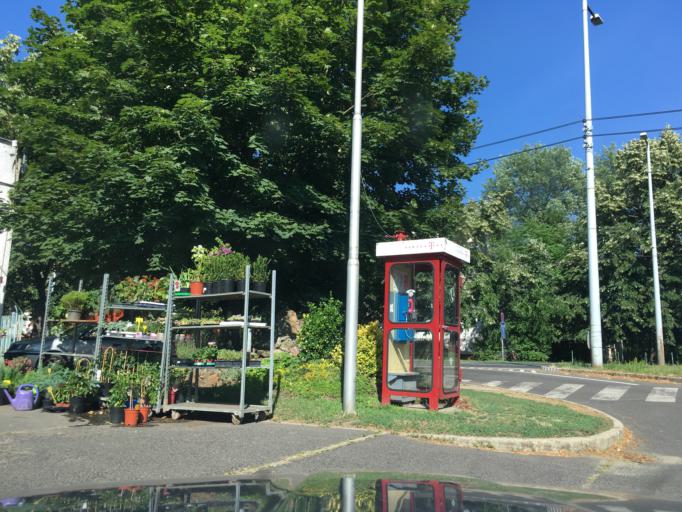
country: HU
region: Hajdu-Bihar
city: Debrecen
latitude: 47.5513
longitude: 21.6480
